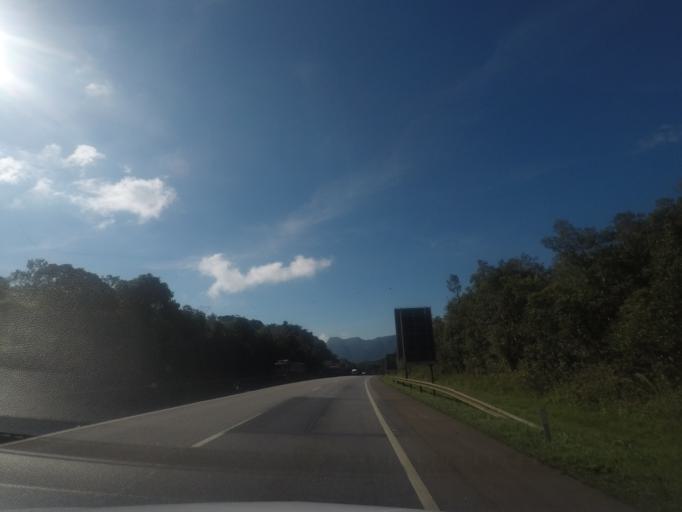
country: BR
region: Parana
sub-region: Piraquara
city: Piraquara
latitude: -25.5903
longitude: -48.9321
